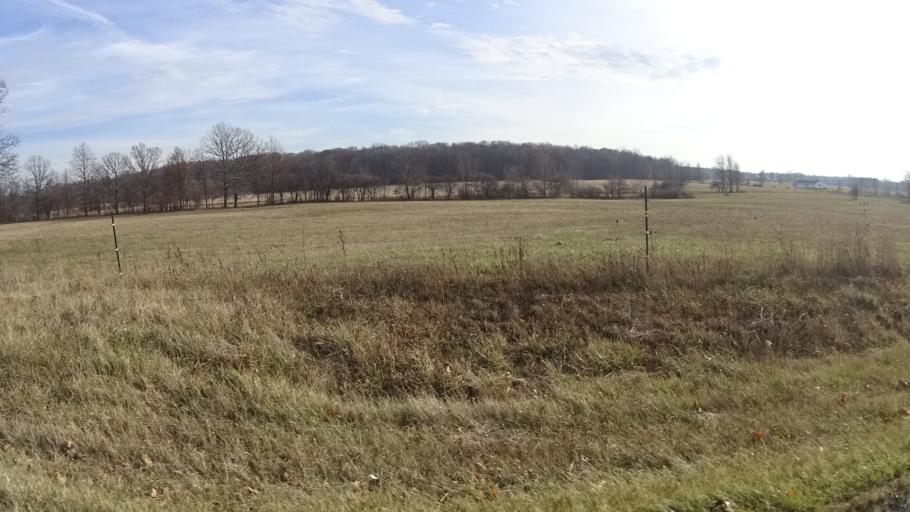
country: US
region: Ohio
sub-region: Lorain County
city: Lagrange
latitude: 41.2022
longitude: -82.0630
